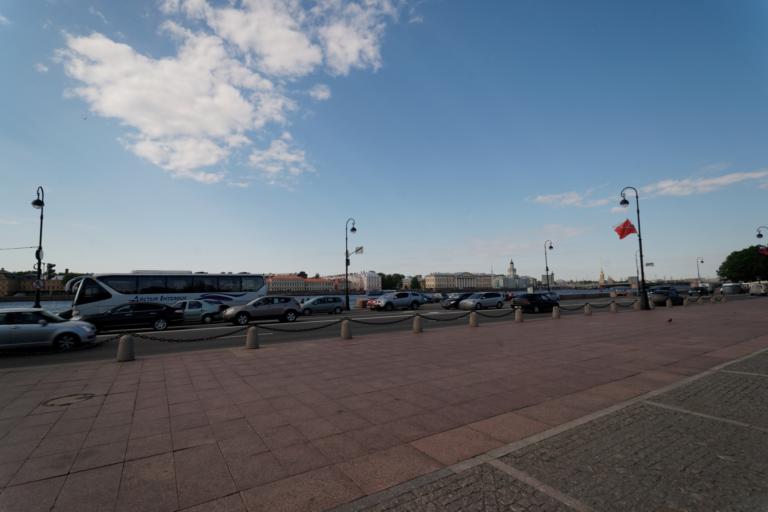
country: RU
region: St.-Petersburg
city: Saint Petersburg
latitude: 59.9365
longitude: 30.3017
